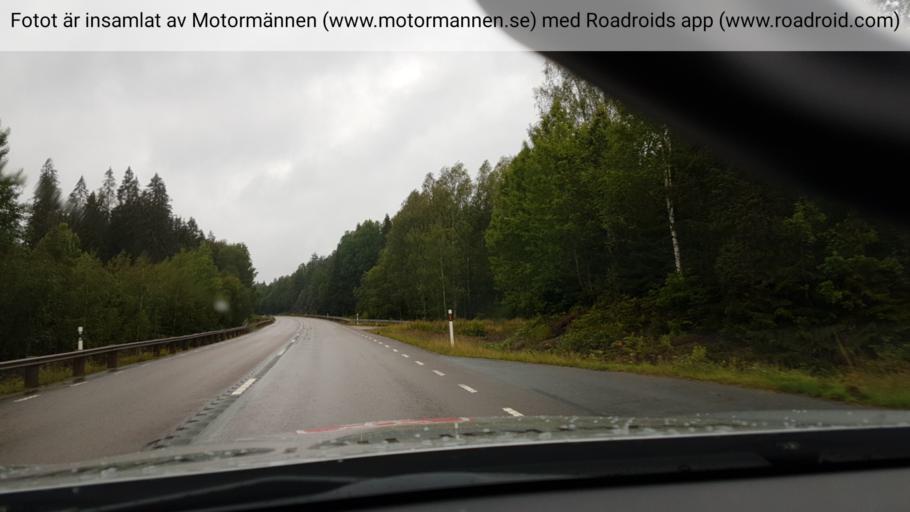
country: SE
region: Vaestra Goetaland
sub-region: Bengtsfors Kommun
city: Billingsfors
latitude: 58.9378
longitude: 12.1940
